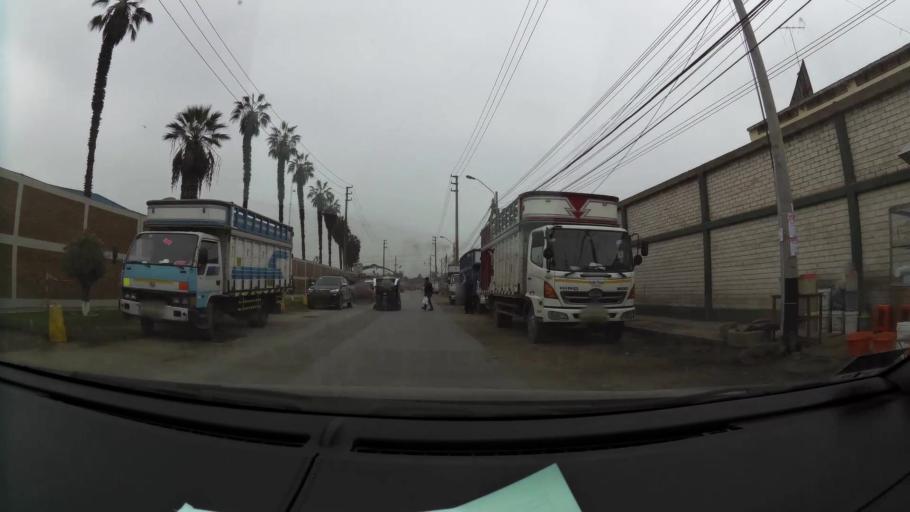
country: PE
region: Lima
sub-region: Lima
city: Carabayllo
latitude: -11.8674
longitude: -77.0721
